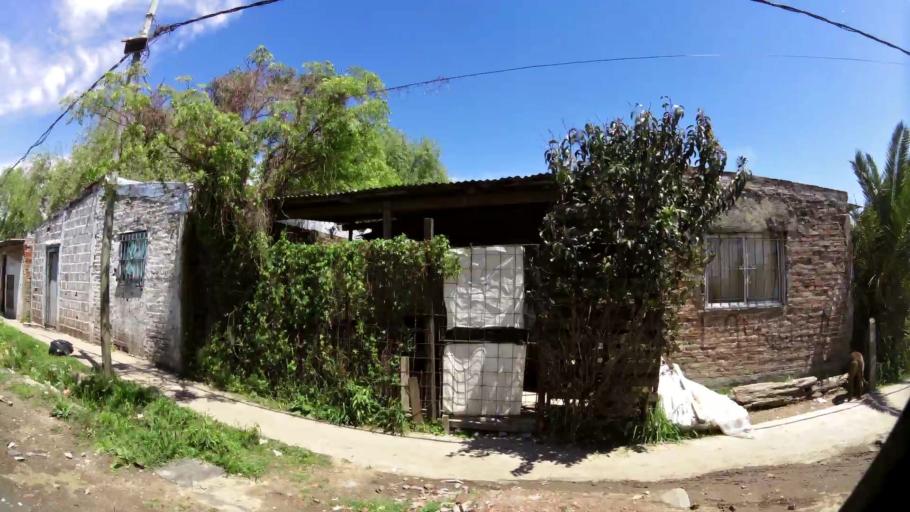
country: AR
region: Buenos Aires
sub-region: Partido de Quilmes
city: Quilmes
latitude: -34.7490
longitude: -58.3100
